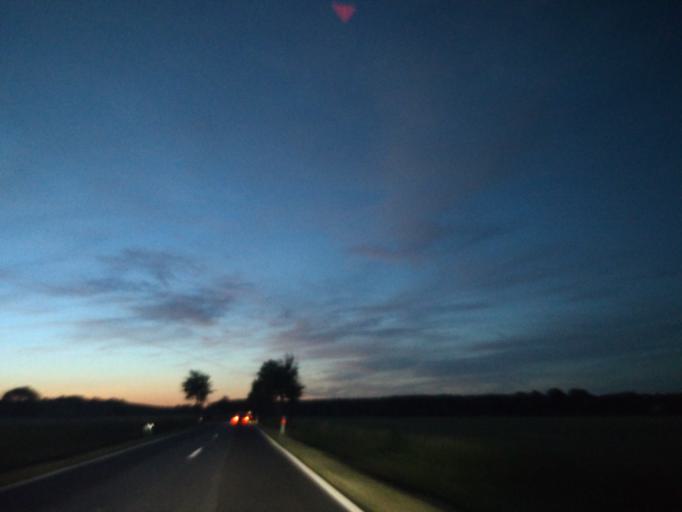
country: HU
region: Vas
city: Vasvar
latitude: 46.9707
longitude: 16.8428
